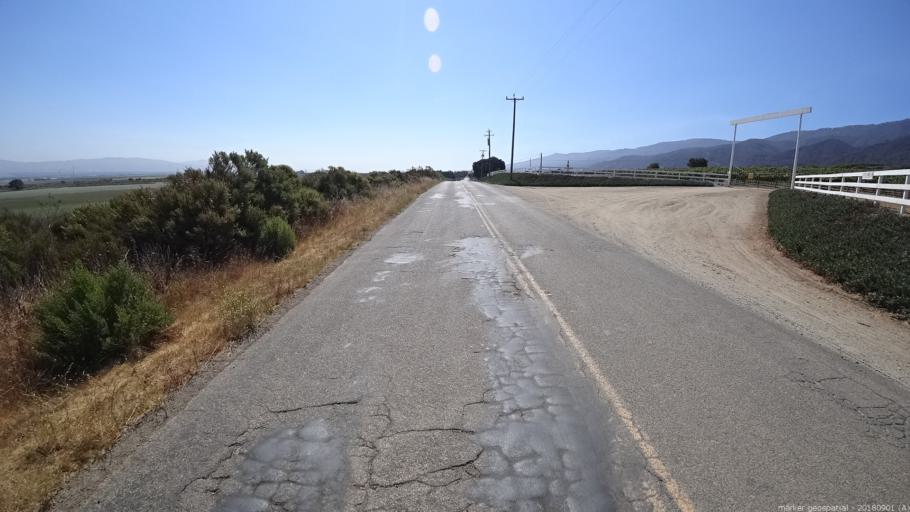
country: US
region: California
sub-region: Monterey County
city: Gonzales
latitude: 36.5018
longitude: -121.5047
